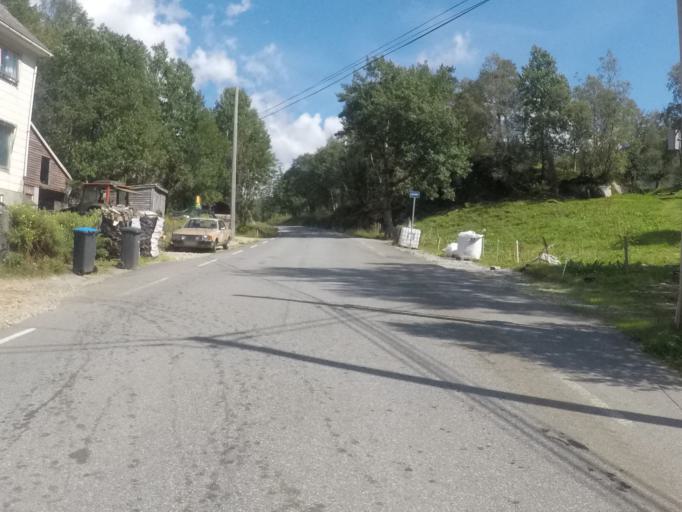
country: NO
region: Sogn og Fjordane
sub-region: Hoyanger
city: Hoyanger
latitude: 61.3196
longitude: 6.2501
